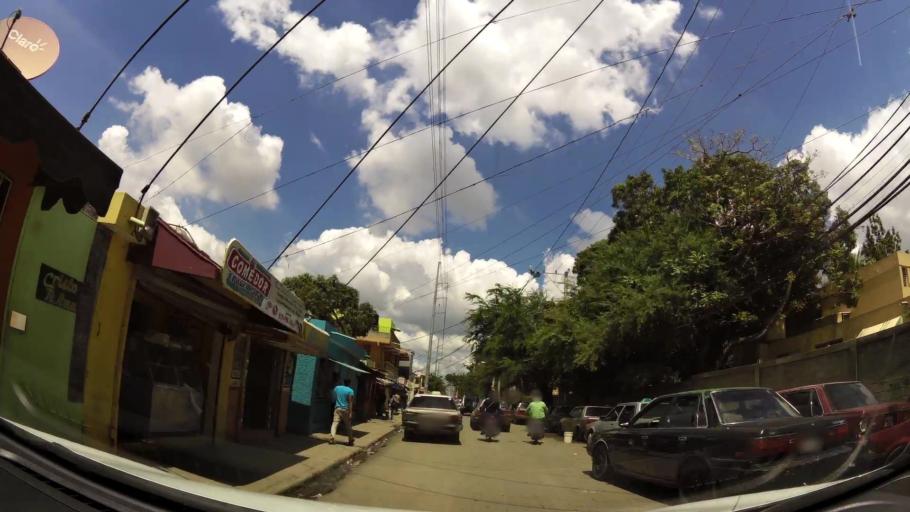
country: DO
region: Santo Domingo
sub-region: Santo Domingo
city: Santo Domingo Este
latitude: 18.5108
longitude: -69.8695
